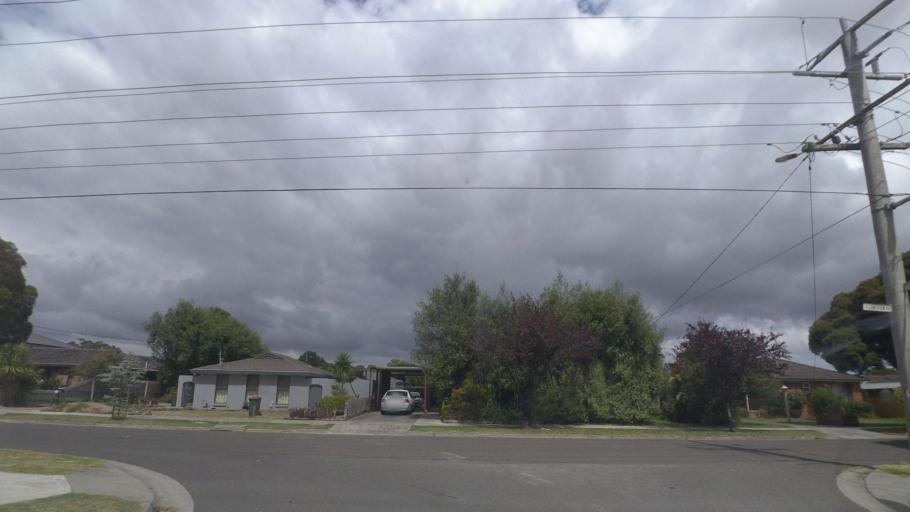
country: AU
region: Victoria
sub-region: Knox
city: Rowville
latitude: -37.9170
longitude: 145.2291
